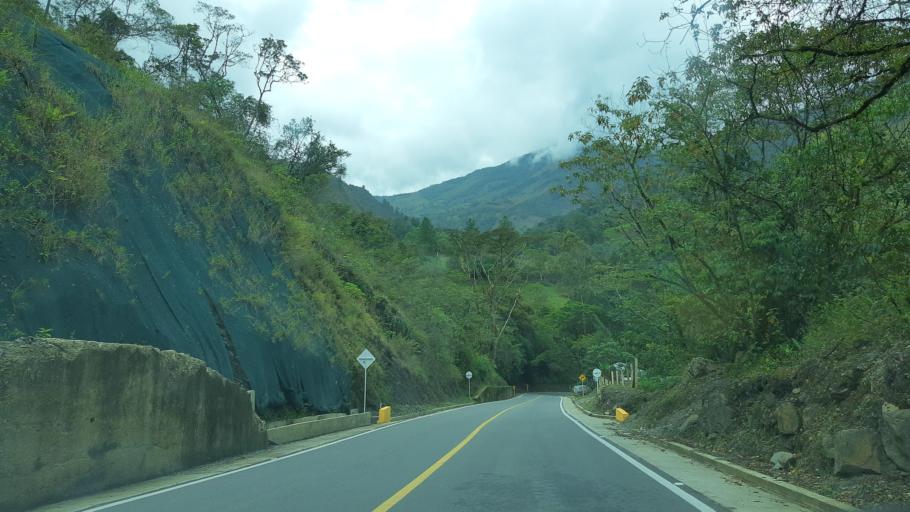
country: CO
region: Boyaca
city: Chivor
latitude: 4.9500
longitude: -73.3059
